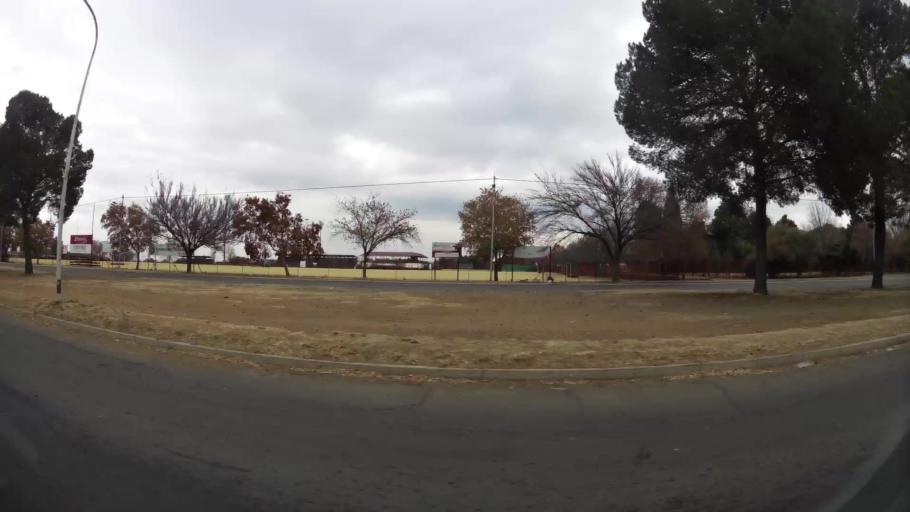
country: ZA
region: Orange Free State
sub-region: Fezile Dabi District Municipality
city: Kroonstad
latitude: -27.6375
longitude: 27.2335
